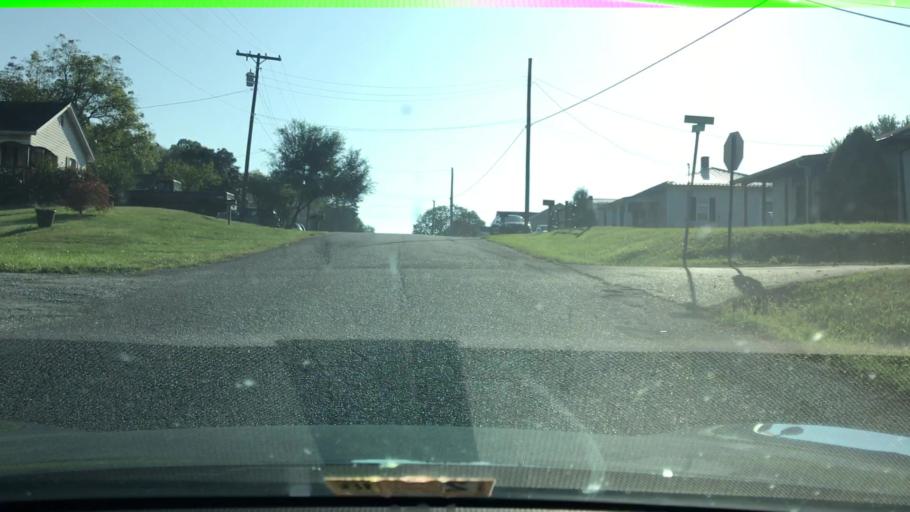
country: US
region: Virginia
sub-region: Pulaski County
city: Pulaski
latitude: 37.0498
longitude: -80.7633
